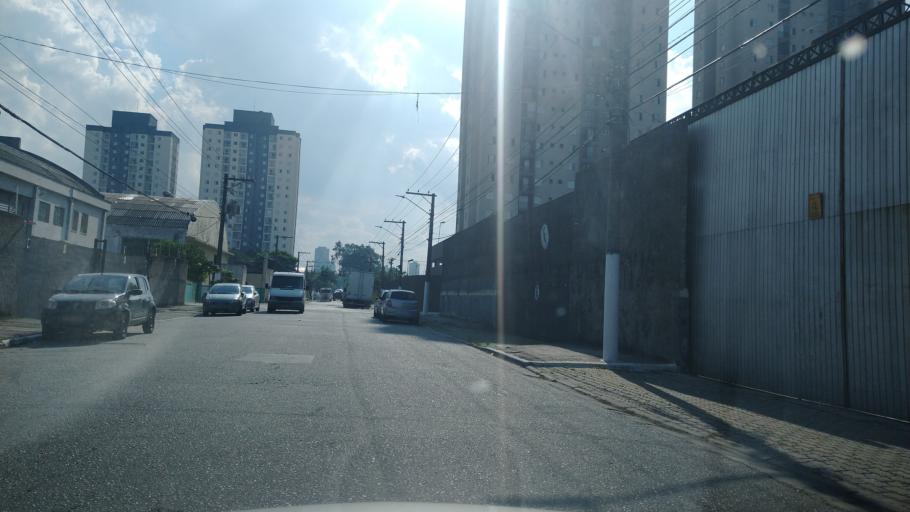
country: BR
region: Sao Paulo
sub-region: Guarulhos
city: Guarulhos
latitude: -23.5128
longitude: -46.5666
